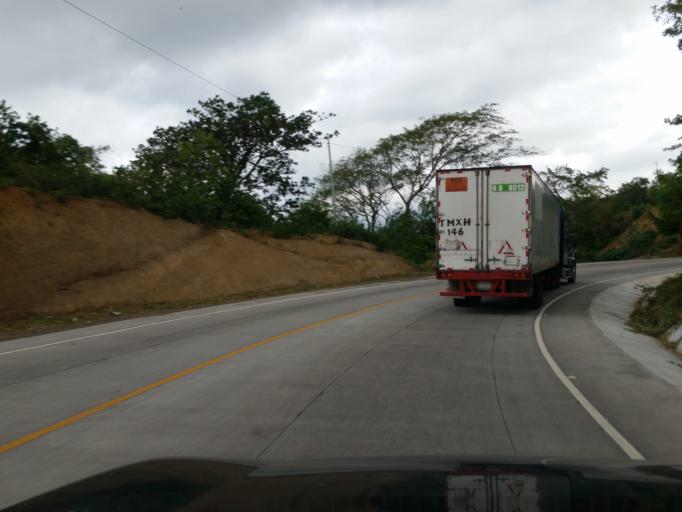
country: NI
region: Managua
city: Ciudad Sandino
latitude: 12.0826
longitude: -86.3787
